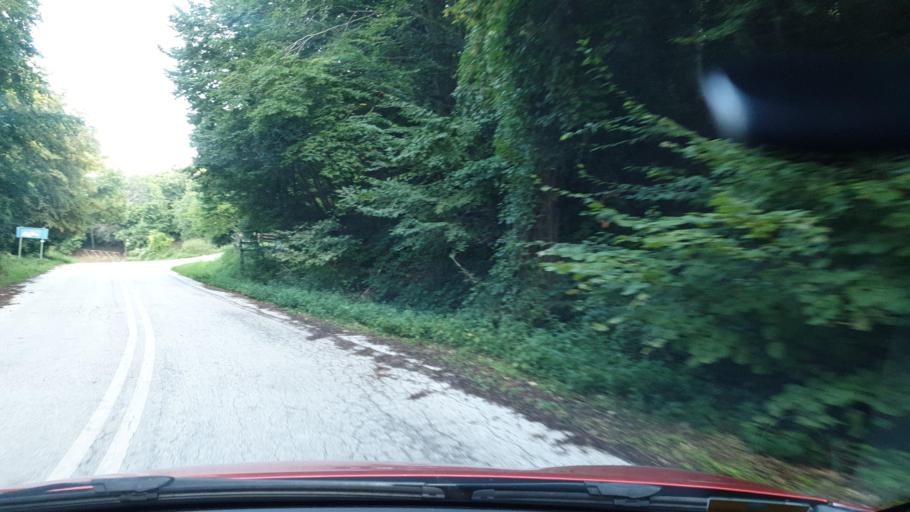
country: GR
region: Central Macedonia
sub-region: Nomos Chalkidikis
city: Galatista
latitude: 40.5080
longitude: 23.2576
